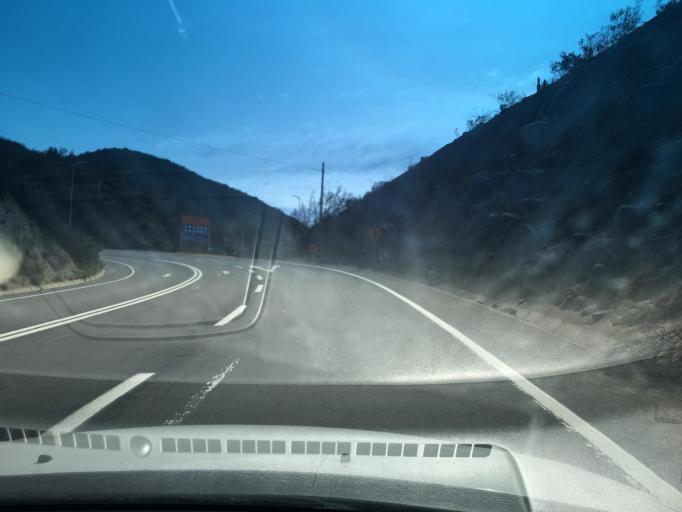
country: CL
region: Valparaiso
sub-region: Provincia de San Felipe
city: Llaillay
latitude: -33.0627
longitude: -70.9966
